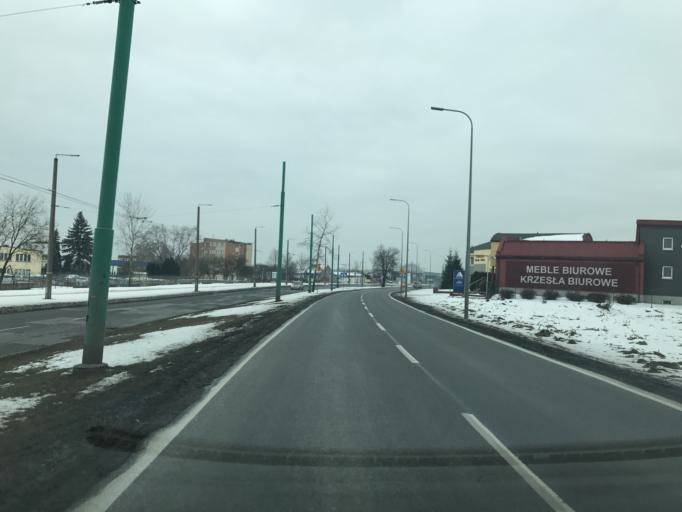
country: PL
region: Silesian Voivodeship
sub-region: Tychy
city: Cielmice
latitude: 50.1021
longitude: 19.0306
